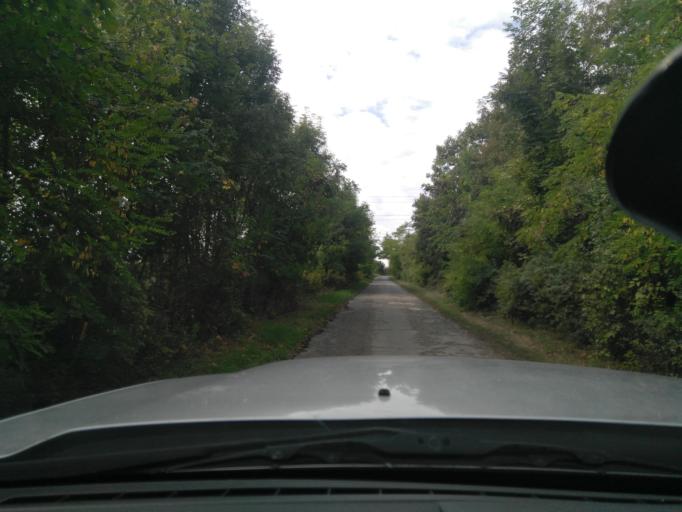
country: HU
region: Fejer
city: Val
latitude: 47.3785
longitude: 18.6901
